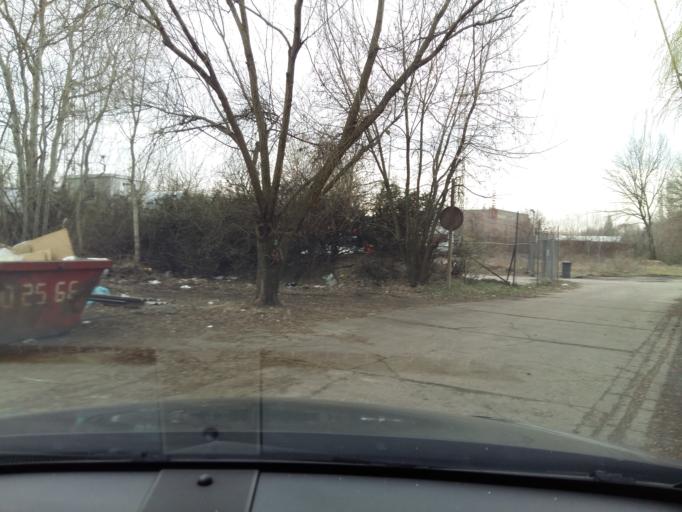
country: HU
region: Budapest
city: Budapest XIII. keruelet
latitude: 47.5372
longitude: 19.0951
